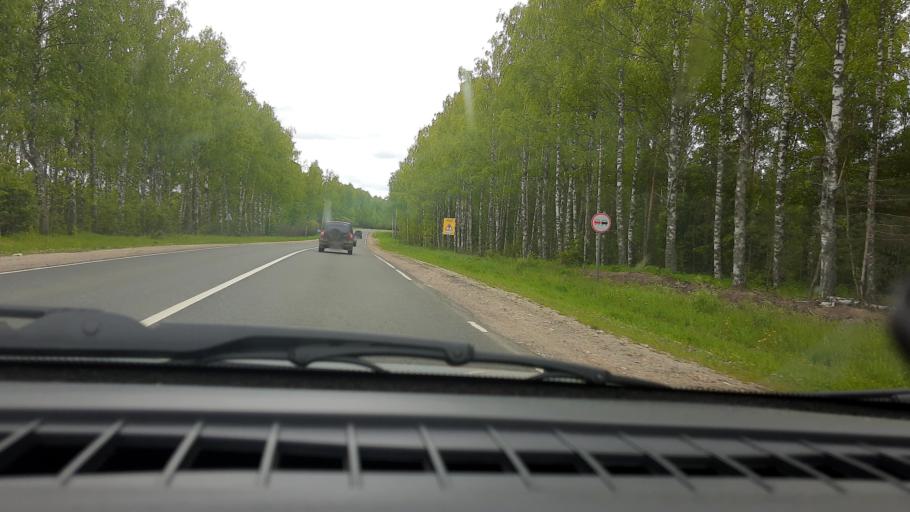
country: RU
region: Nizjnij Novgorod
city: Krasnyye Baki
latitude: 57.0770
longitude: 45.1439
